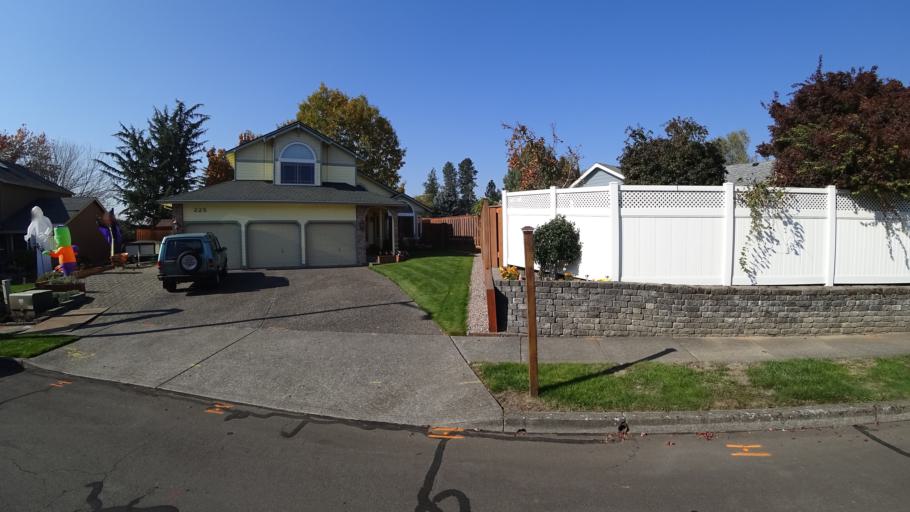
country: US
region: Oregon
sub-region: Multnomah County
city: Gresham
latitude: 45.4954
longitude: -122.4533
